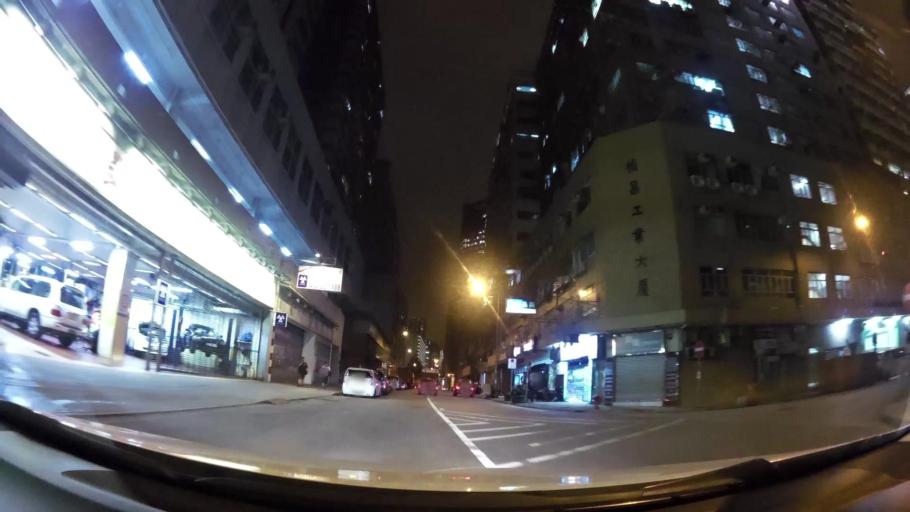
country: HK
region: Tsuen Wan
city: Tsuen Wan
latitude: 22.3648
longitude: 114.1343
